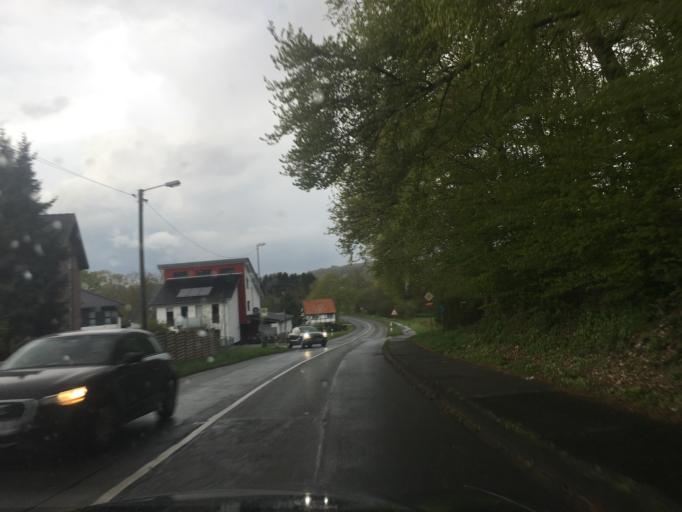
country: DE
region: North Rhine-Westphalia
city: Leichlingen
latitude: 51.1201
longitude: 7.0022
